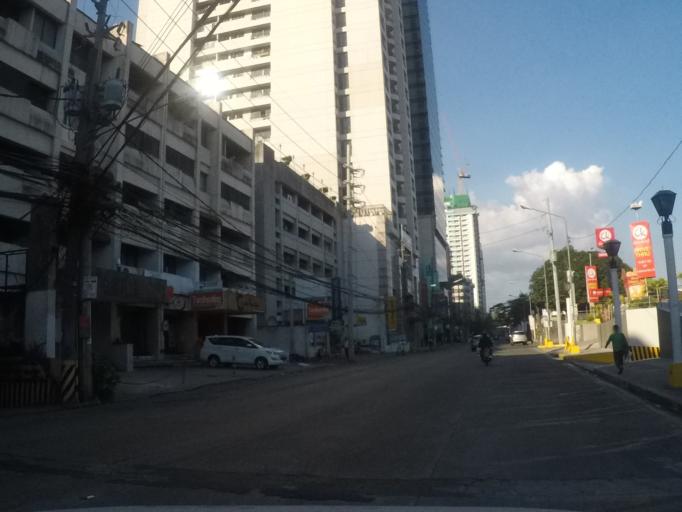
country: PH
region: Metro Manila
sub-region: San Juan
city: San Juan
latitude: 14.6040
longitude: 121.0521
